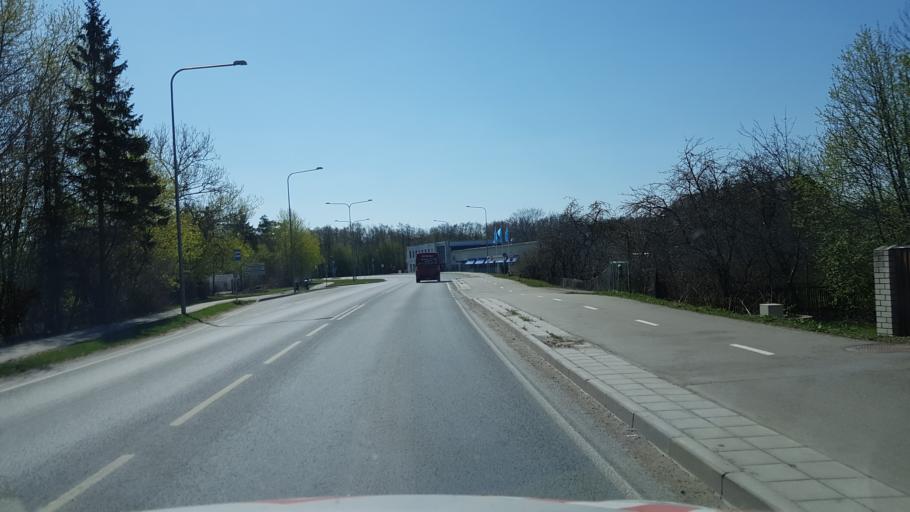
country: EE
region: Harju
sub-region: Viimsi vald
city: Haabneeme
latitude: 59.5086
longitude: 24.8225
